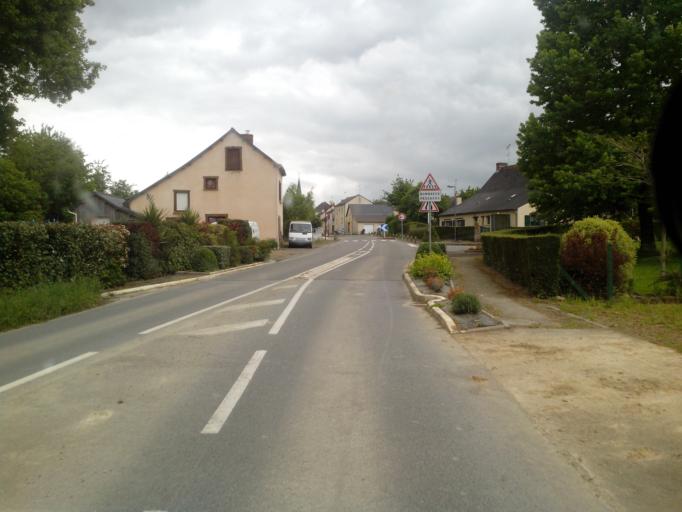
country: FR
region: Brittany
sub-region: Departement d'Ille-et-Vilaine
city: Chasne-sur-Illet
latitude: 48.2433
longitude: -1.5660
